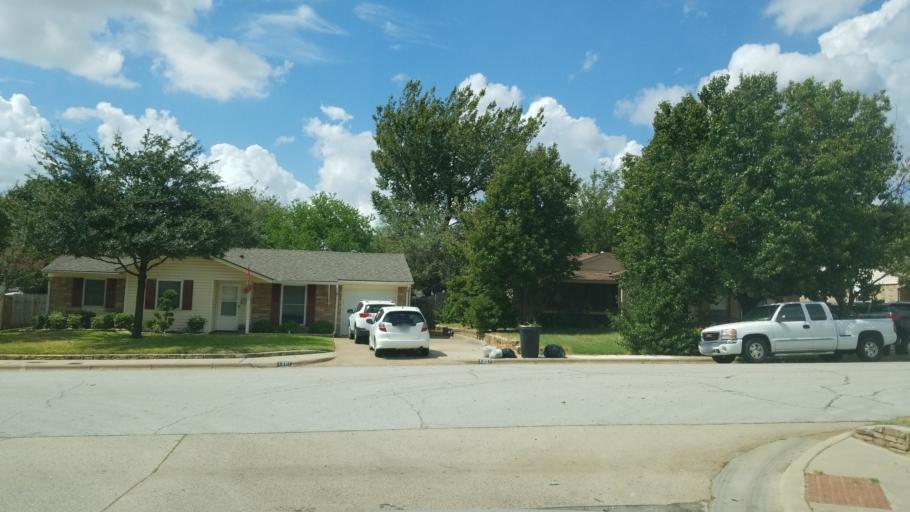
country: US
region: Texas
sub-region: Tarrant County
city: Euless
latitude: 32.8541
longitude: -97.0901
